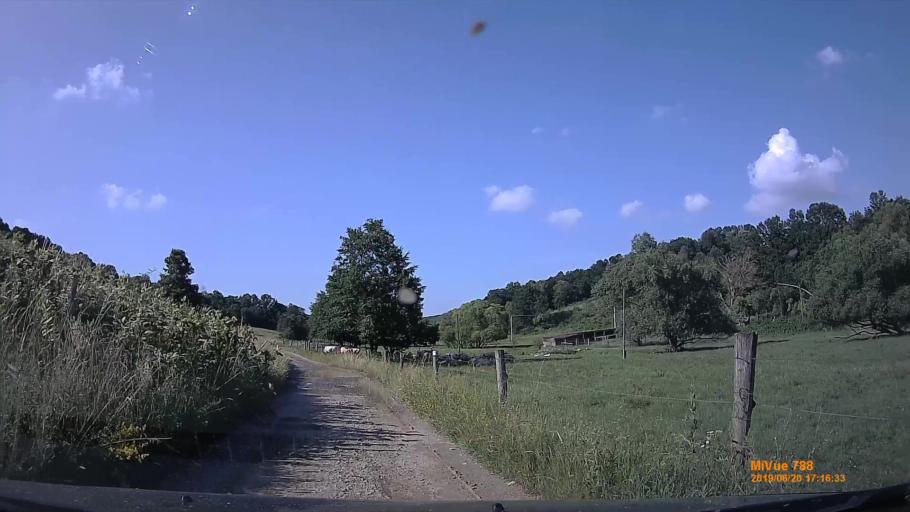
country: HU
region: Baranya
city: Buekkoesd
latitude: 46.1549
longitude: 18.0101
